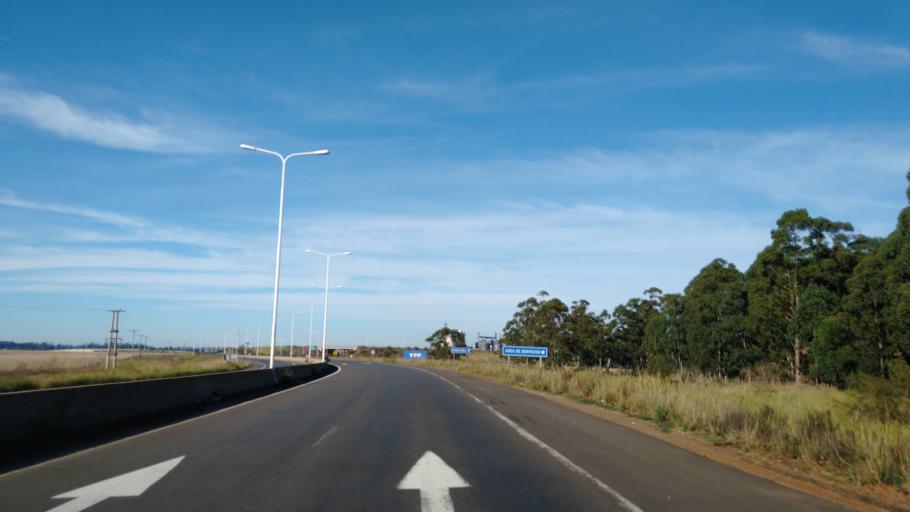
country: AR
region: Corrientes
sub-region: Departamento de Paso de los Libres
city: Paso de los Libres
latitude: -29.7065
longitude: -57.2103
